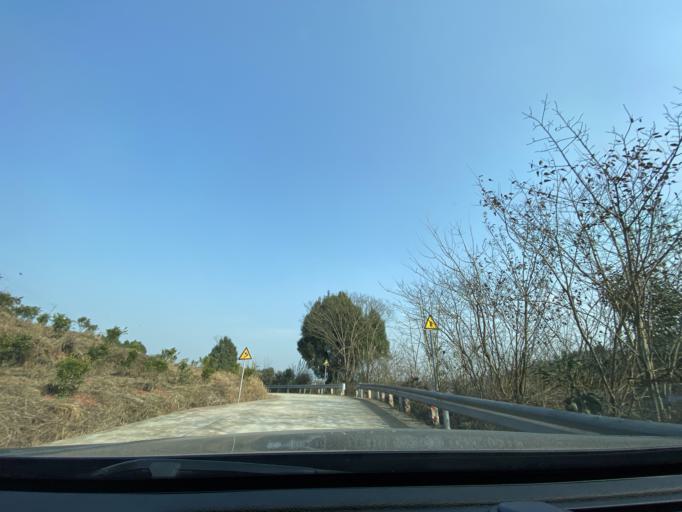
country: CN
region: Sichuan
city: Wenlin
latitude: 30.2508
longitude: 104.2522
